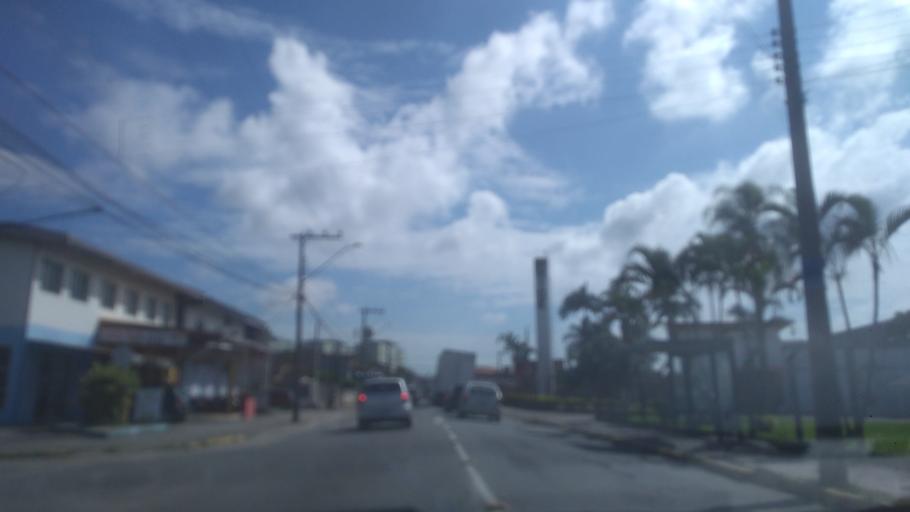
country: BR
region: Santa Catarina
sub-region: Joinville
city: Joinville
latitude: -26.3041
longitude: -48.8246
